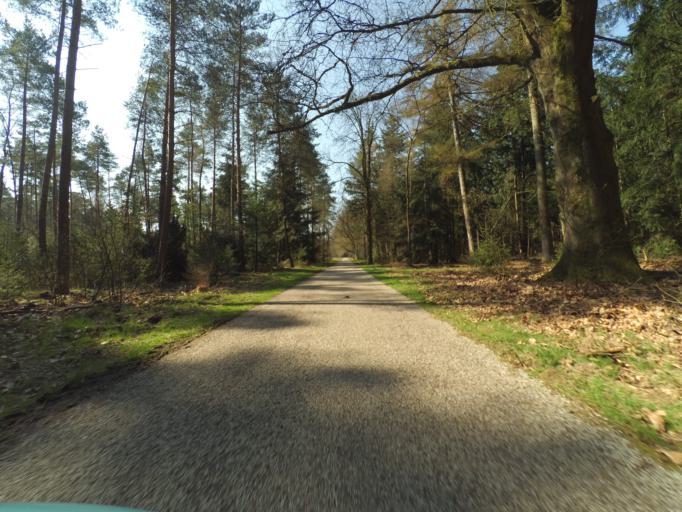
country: NL
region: Gelderland
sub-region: Gemeente Ede
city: Otterlo
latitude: 52.1042
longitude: 5.8401
